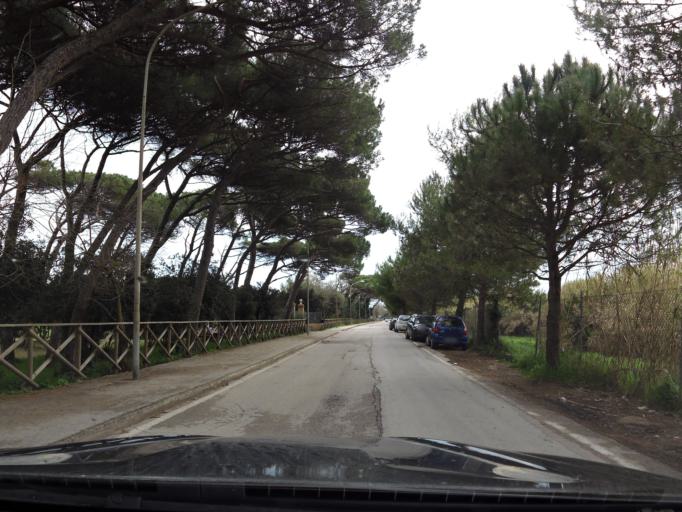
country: IT
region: The Marches
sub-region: Provincia di Macerata
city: Porto Recanati
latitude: 43.4203
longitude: 13.6705
